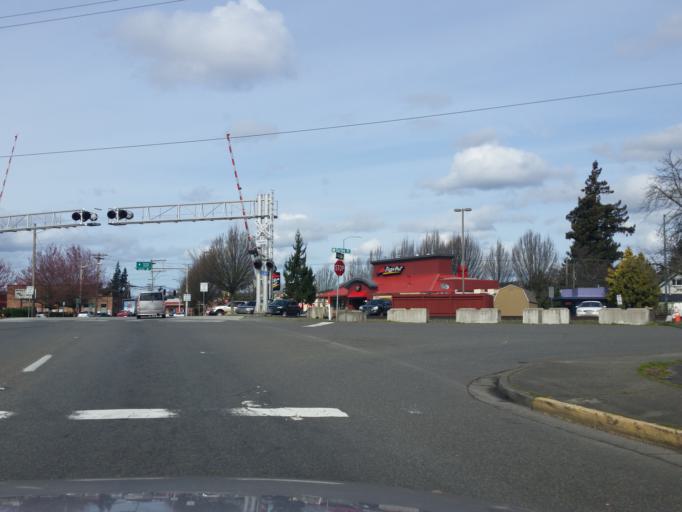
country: US
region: Washington
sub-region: Pierce County
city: Puyallup
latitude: 47.1915
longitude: -122.2914
